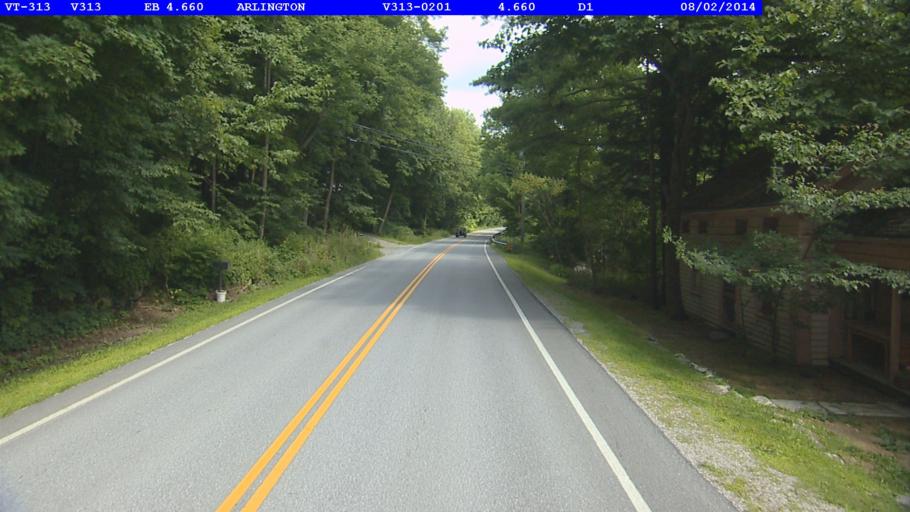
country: US
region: Vermont
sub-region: Bennington County
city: Arlington
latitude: 43.0842
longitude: -73.1887
